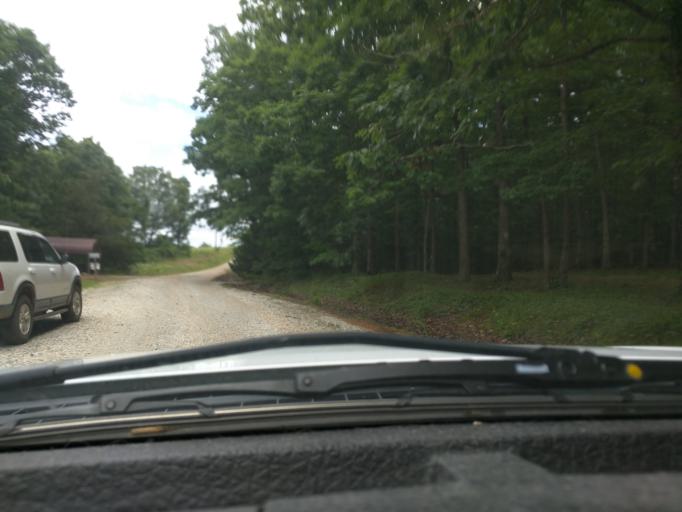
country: US
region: Arkansas
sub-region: Madison County
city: Huntsville
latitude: 35.8825
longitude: -93.5497
